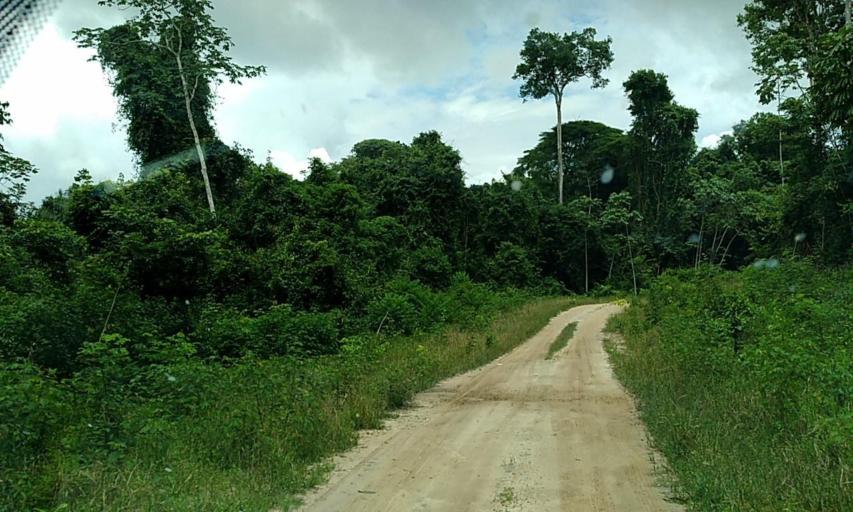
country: BR
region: Para
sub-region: Altamira
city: Altamira
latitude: -3.0555
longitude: -52.9098
